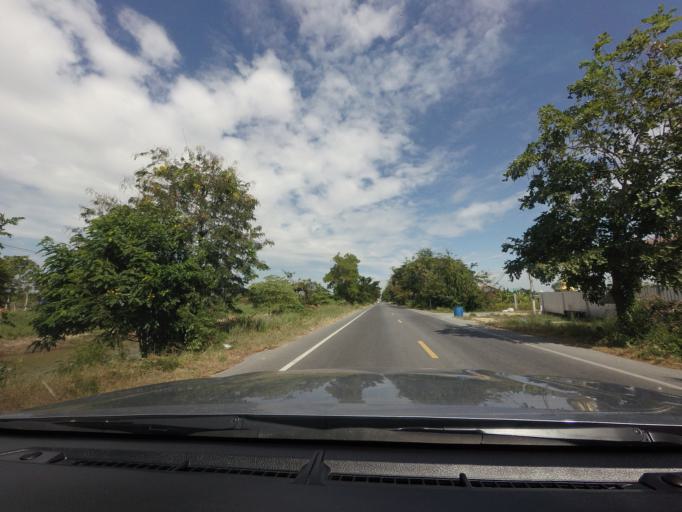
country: TH
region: Suphan Buri
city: Suphan Buri
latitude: 14.4570
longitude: 100.0860
